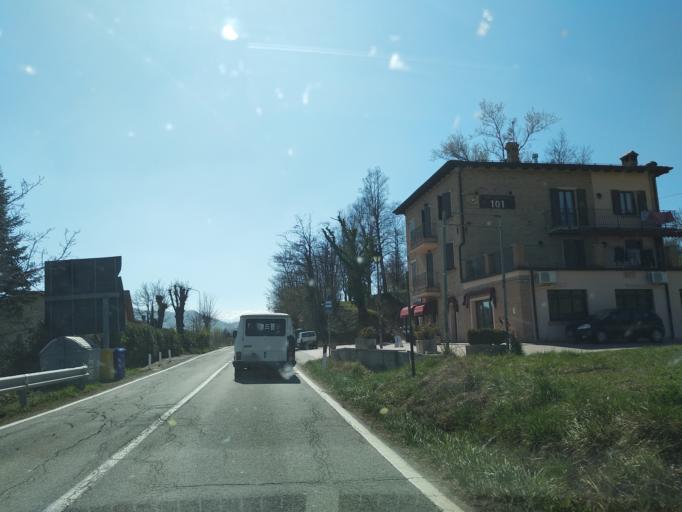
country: IT
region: Emilia-Romagna
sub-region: Provincia di Reggio Emilia
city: Carpineti
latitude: 44.4703
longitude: 10.4896
